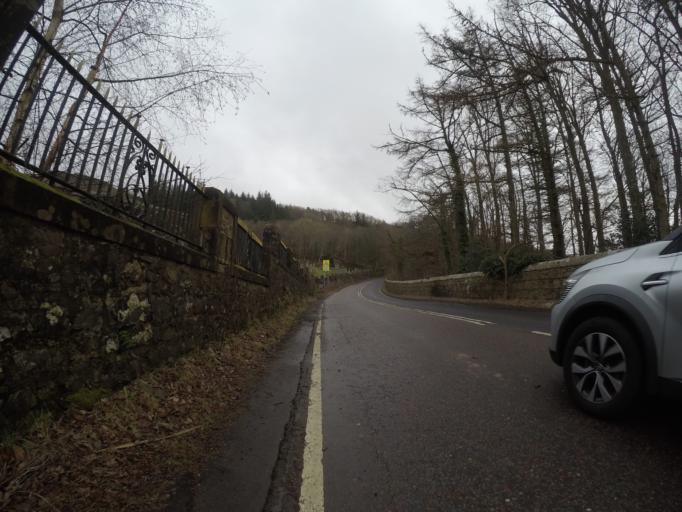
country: GB
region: Scotland
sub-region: North Ayrshire
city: Largs
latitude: 55.7844
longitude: -4.8549
